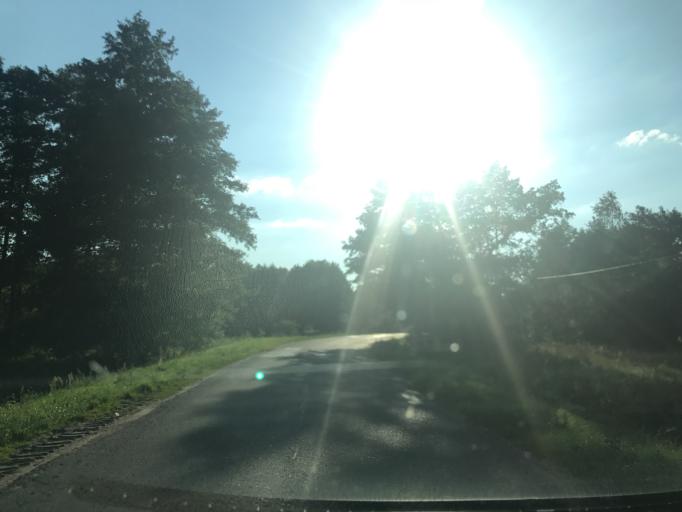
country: PL
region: Greater Poland Voivodeship
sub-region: Powiat turecki
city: Wladyslawow
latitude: 52.0998
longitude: 18.4036
